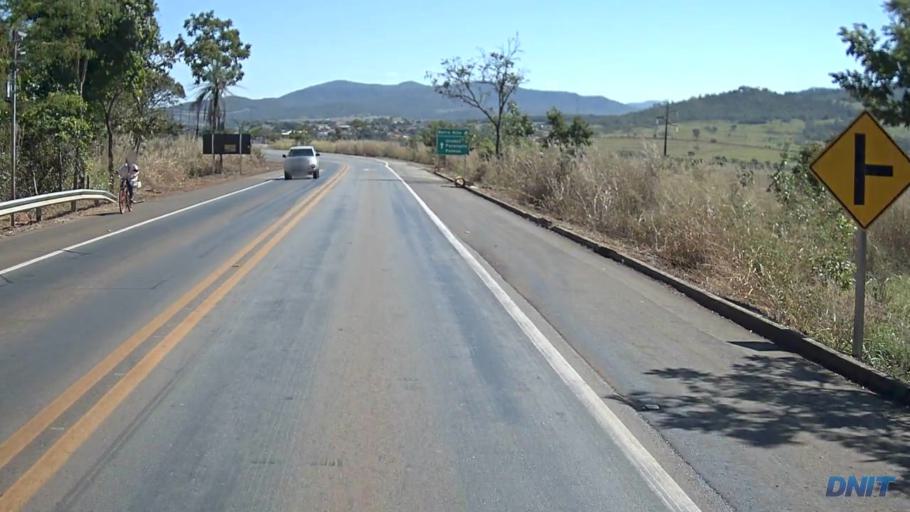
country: BR
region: Goias
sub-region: Barro Alto
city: Barro Alto
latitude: -14.9913
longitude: -48.9083
